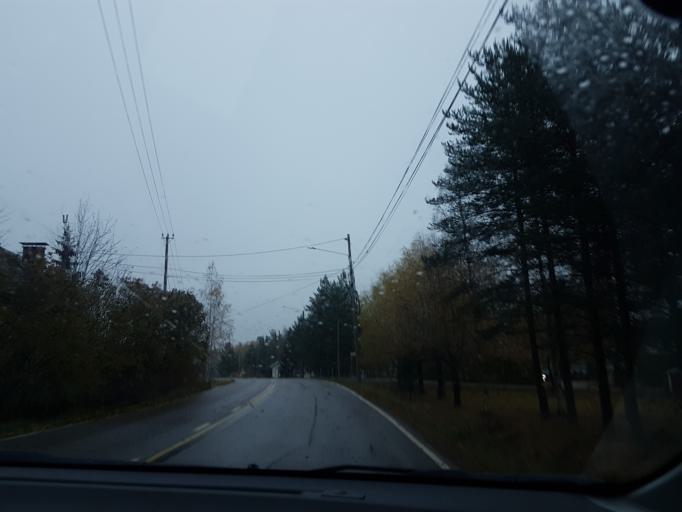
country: FI
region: Uusimaa
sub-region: Helsinki
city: Maentsaelae
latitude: 60.6181
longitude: 25.2598
